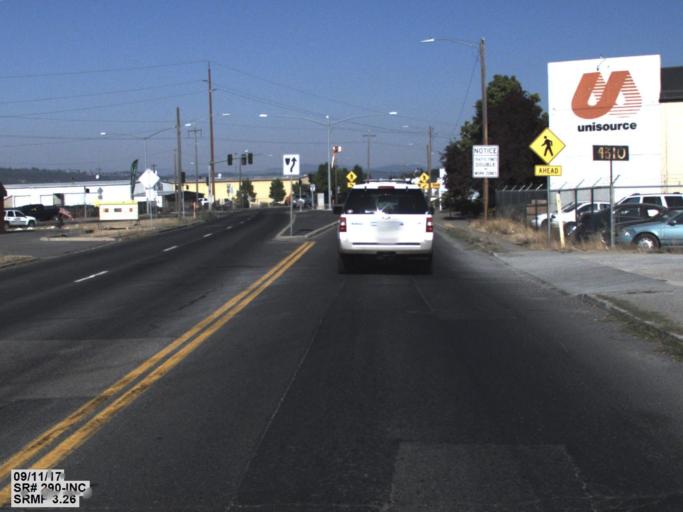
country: US
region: Washington
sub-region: Spokane County
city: Millwood
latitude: 47.6712
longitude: -117.3460
